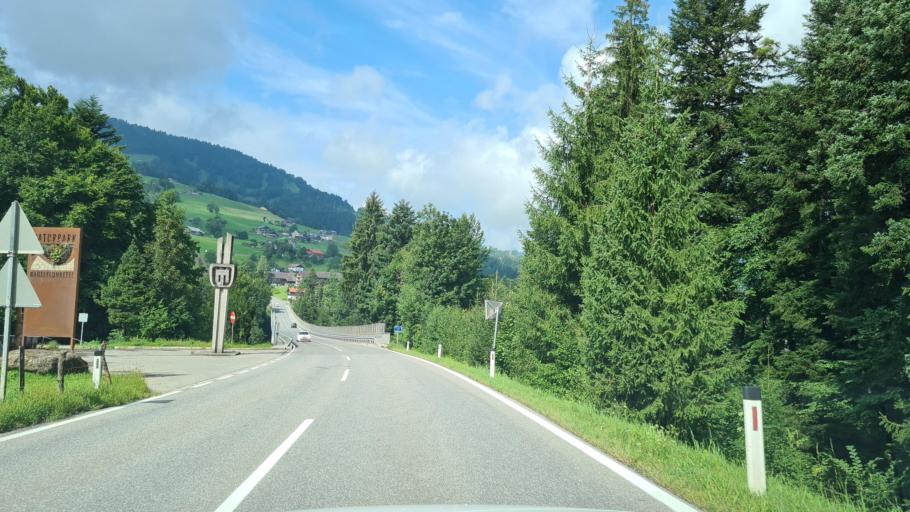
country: AT
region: Vorarlberg
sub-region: Politischer Bezirk Bregenz
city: Egg
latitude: 47.4525
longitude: 9.8911
